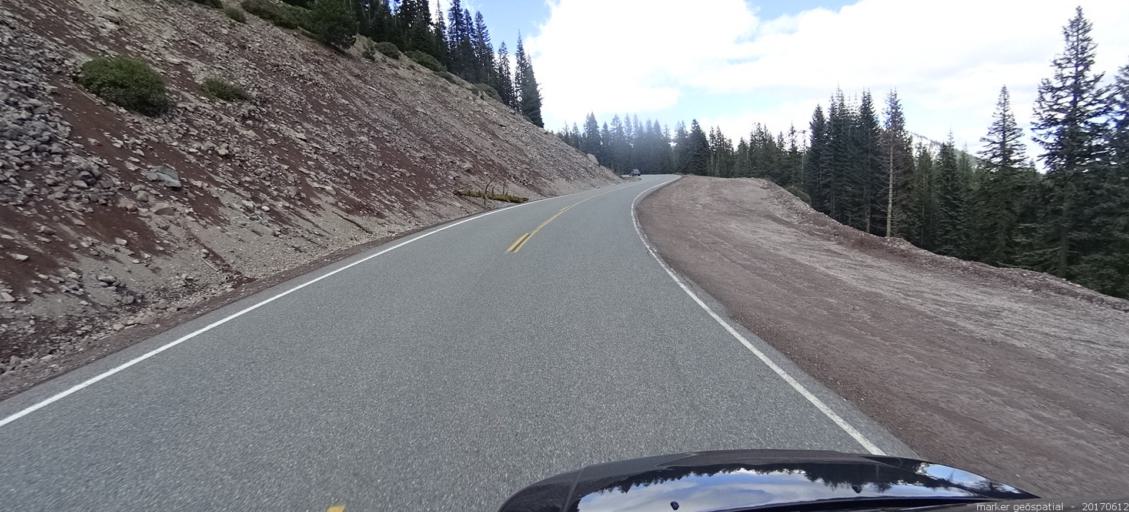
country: US
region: California
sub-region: Siskiyou County
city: Mount Shasta
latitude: 41.3515
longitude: -122.2380
